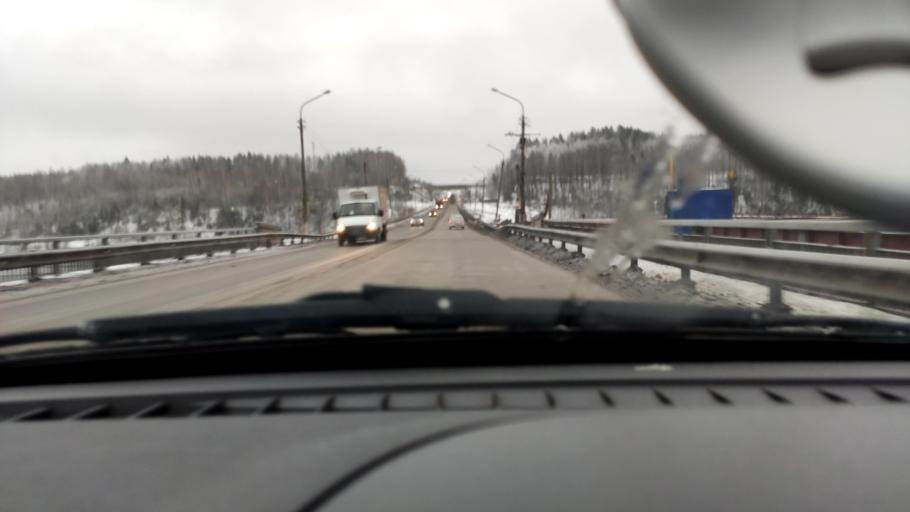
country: RU
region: Perm
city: Polazna
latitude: 58.1580
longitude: 56.4173
